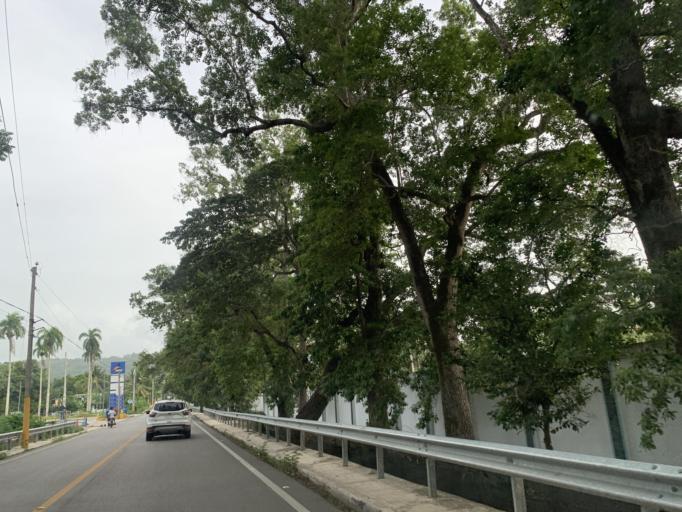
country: DO
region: Puerto Plata
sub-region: Puerto Plata
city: Puerto Plata
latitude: 19.7039
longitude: -70.6247
